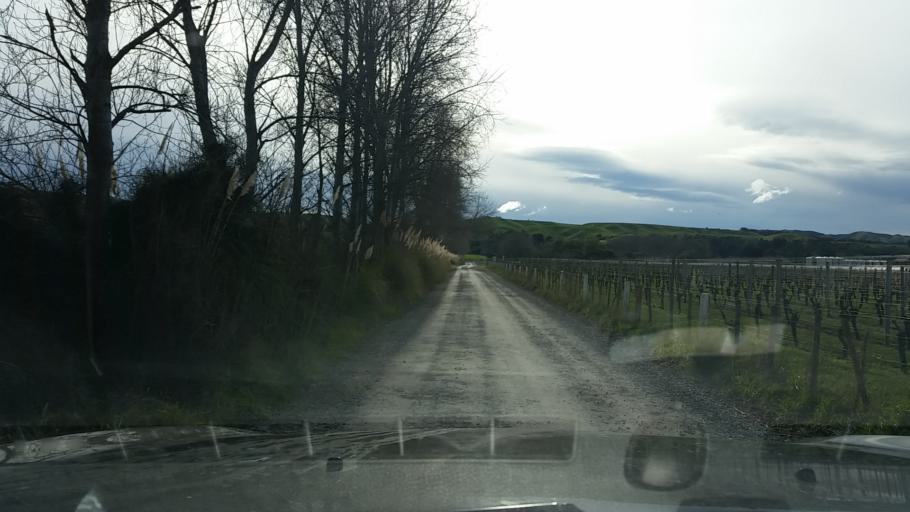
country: NZ
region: Marlborough
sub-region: Marlborough District
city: Blenheim
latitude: -41.6240
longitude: 174.0997
